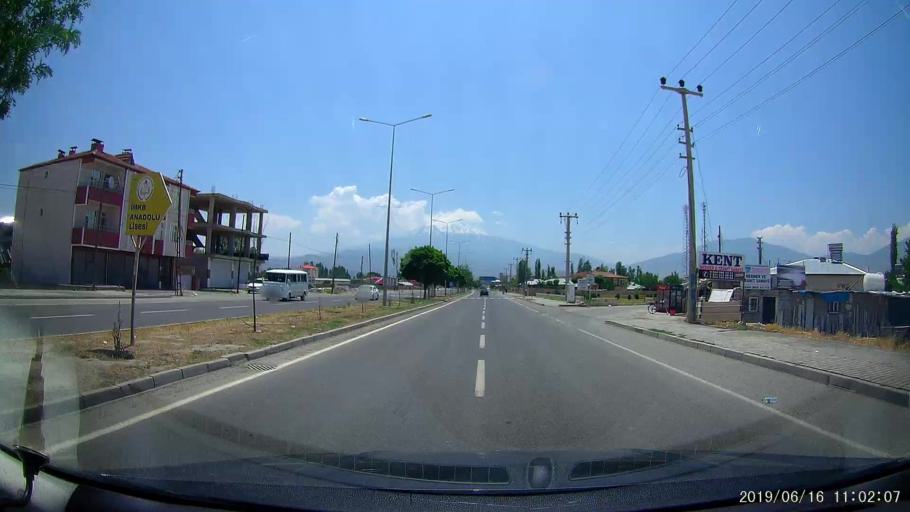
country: TR
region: Igdir
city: Igdir
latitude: 39.9094
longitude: 44.0568
